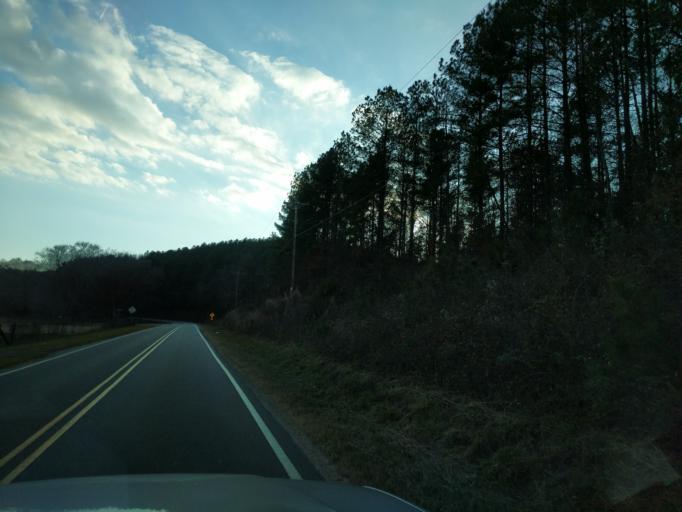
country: US
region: North Carolina
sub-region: Rutherford County
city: Rutherfordton
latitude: 35.2841
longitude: -82.0287
